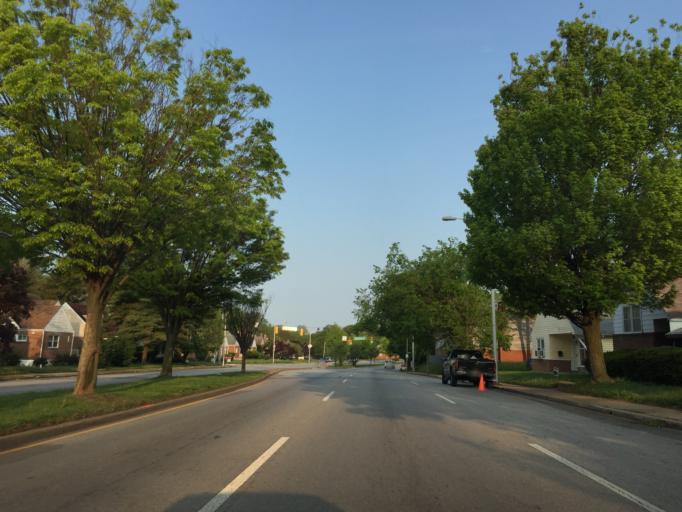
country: US
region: Maryland
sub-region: Baltimore County
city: Lochearn
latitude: 39.3429
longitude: -76.6903
